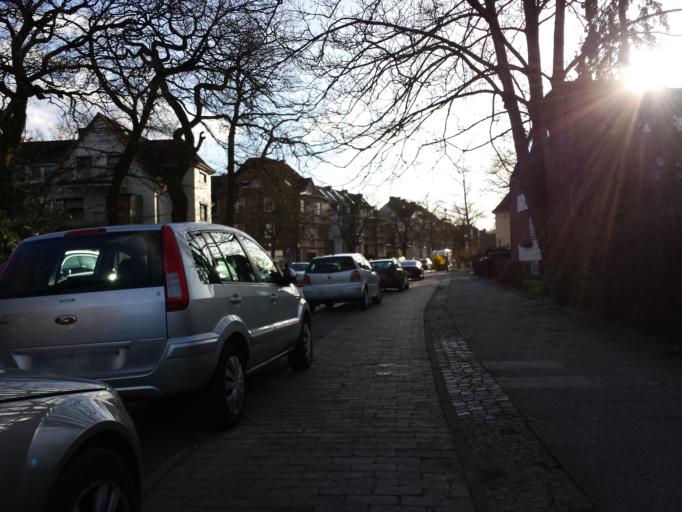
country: DE
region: Bremen
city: Bremen
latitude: 53.0881
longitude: 8.8507
